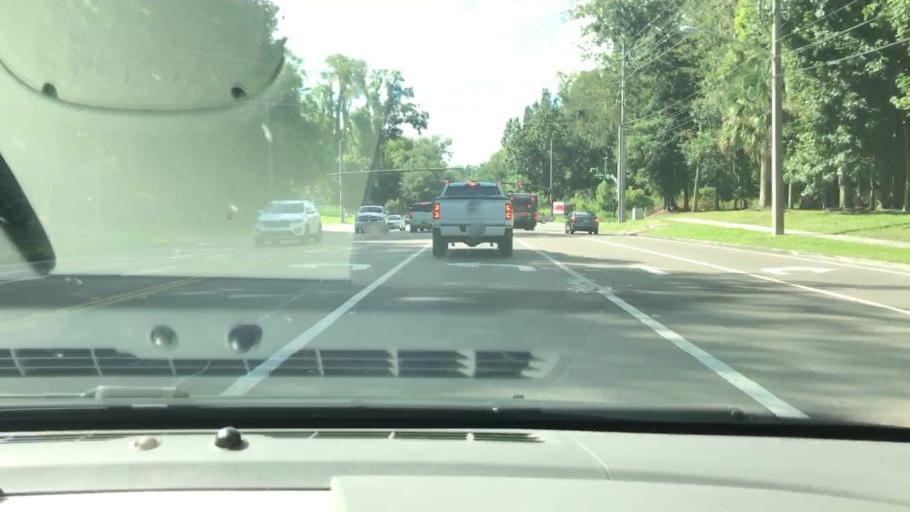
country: US
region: Florida
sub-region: Alachua County
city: Gainesville
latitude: 29.6408
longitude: -82.3982
